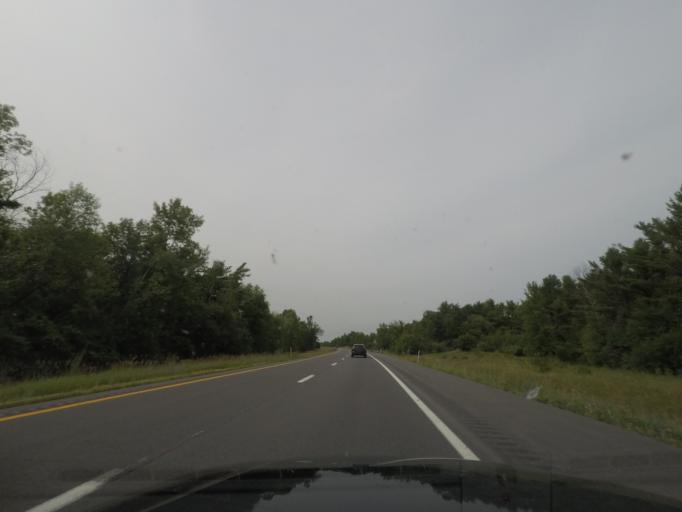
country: US
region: New York
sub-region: Clinton County
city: Cumberland Head
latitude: 44.7499
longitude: -73.4272
